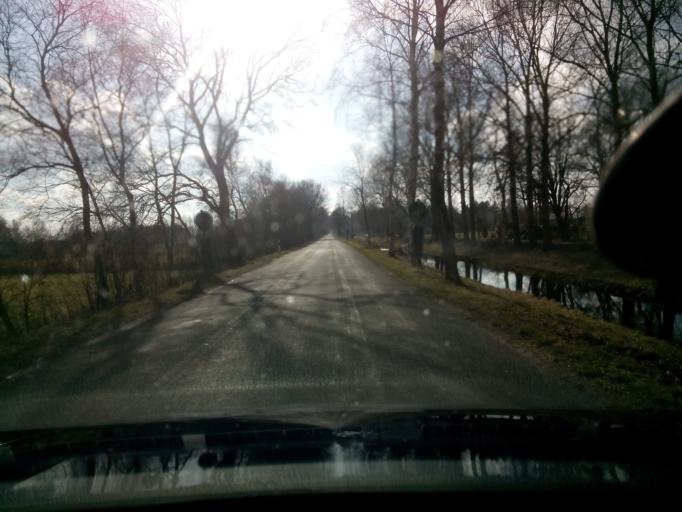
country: DE
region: Lower Saxony
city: Gnarrenburg
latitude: 53.3694
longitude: 9.0087
